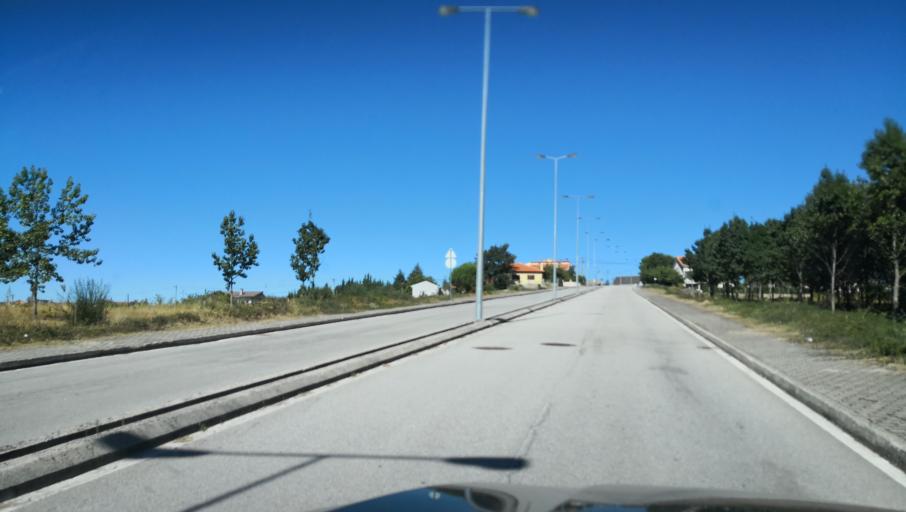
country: PT
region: Vila Real
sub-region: Valpacos
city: Valpacos
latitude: 41.6564
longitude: -7.3190
